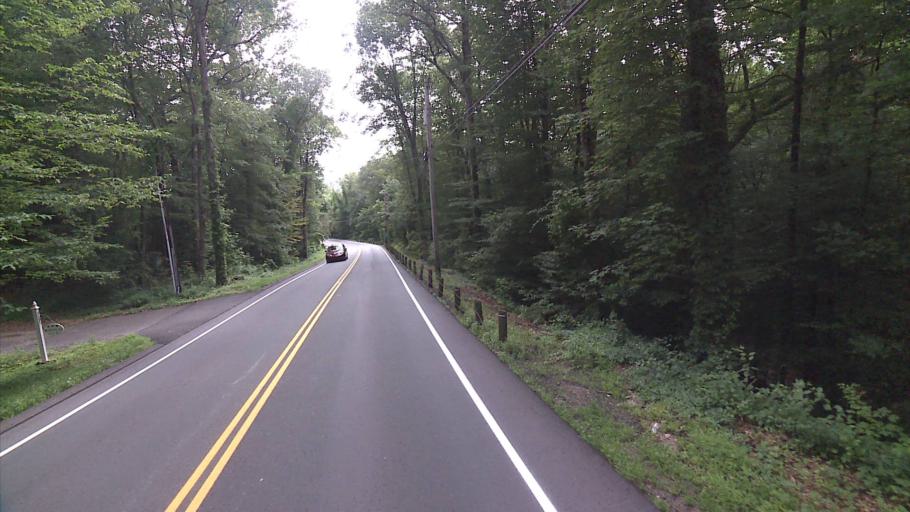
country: US
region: Connecticut
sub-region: New Haven County
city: Heritage Village
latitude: 41.5127
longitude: -73.2527
